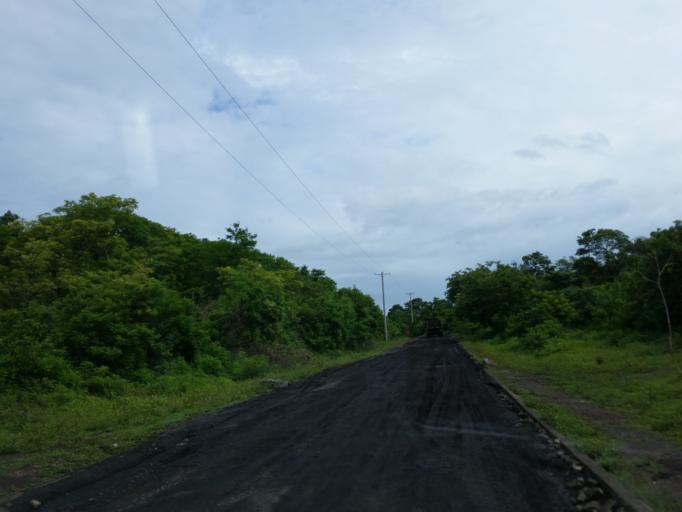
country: NI
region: Leon
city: La Paz Centro
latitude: 12.3753
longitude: -86.6621
